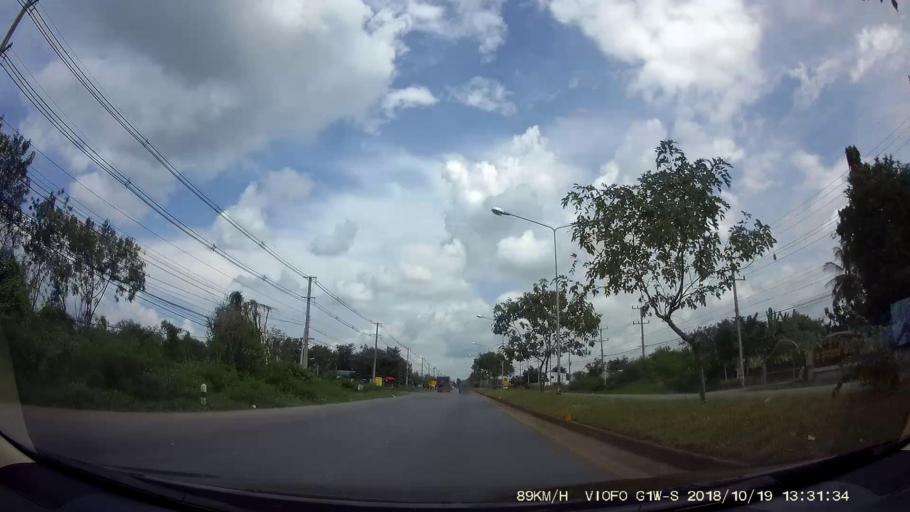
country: TH
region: Chaiyaphum
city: Chatturat
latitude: 15.5777
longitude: 101.8693
